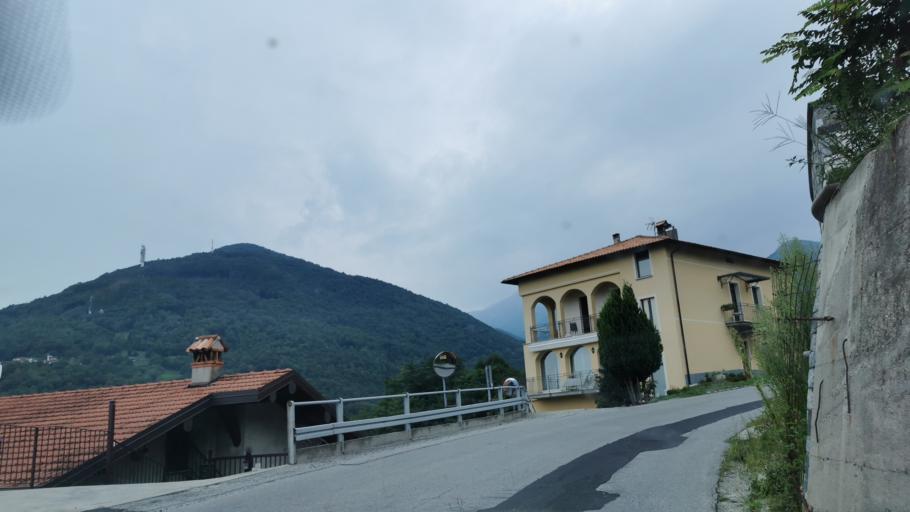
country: IT
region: Lombardy
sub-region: Provincia di Como
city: Gravedona-San Gregorio
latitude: 46.1529
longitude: 9.2980
